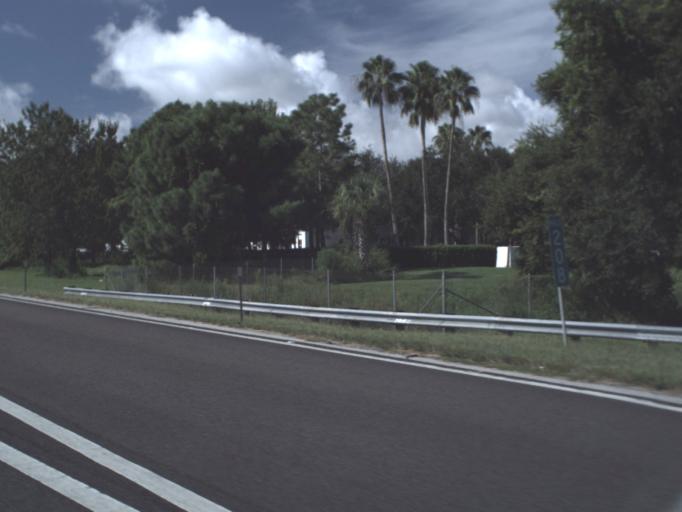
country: US
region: Florida
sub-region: Sarasota County
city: Lake Sarasota
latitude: 27.3033
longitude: -82.4484
